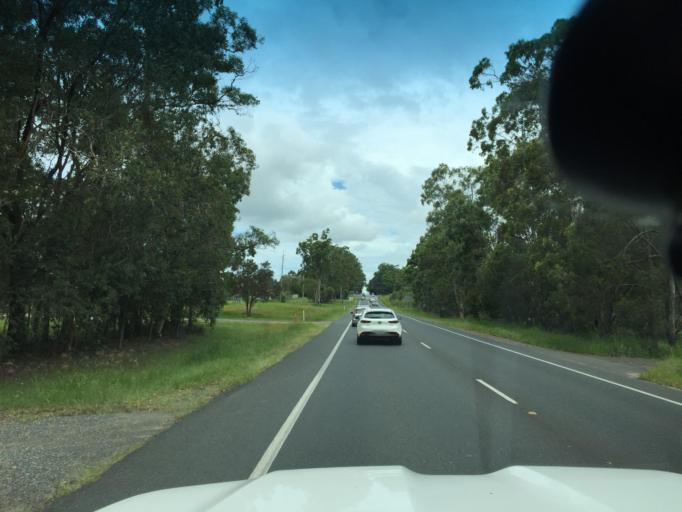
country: AU
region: Queensland
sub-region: Moreton Bay
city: Deception Bay
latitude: -27.1826
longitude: 152.9992
